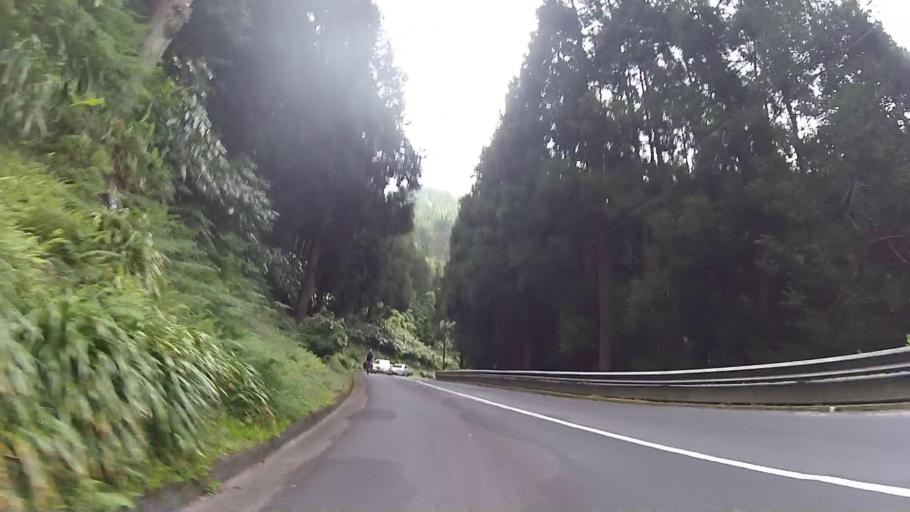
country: PT
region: Azores
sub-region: Povoacao
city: Furnas
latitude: 37.7638
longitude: -25.2879
